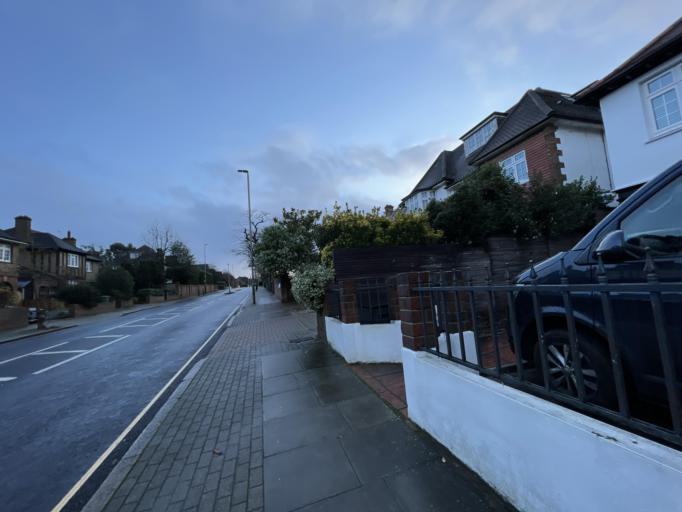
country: GB
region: England
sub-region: Greater London
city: Wandsworth
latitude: 51.4554
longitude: -0.2372
